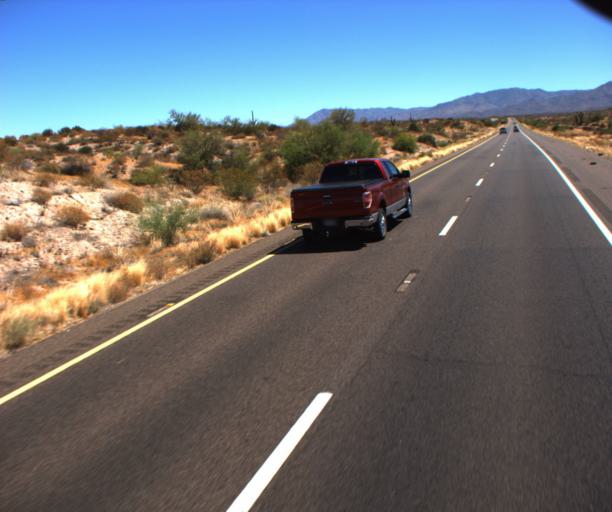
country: US
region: Arizona
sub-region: Maricopa County
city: Rio Verde
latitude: 33.6360
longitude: -111.5466
